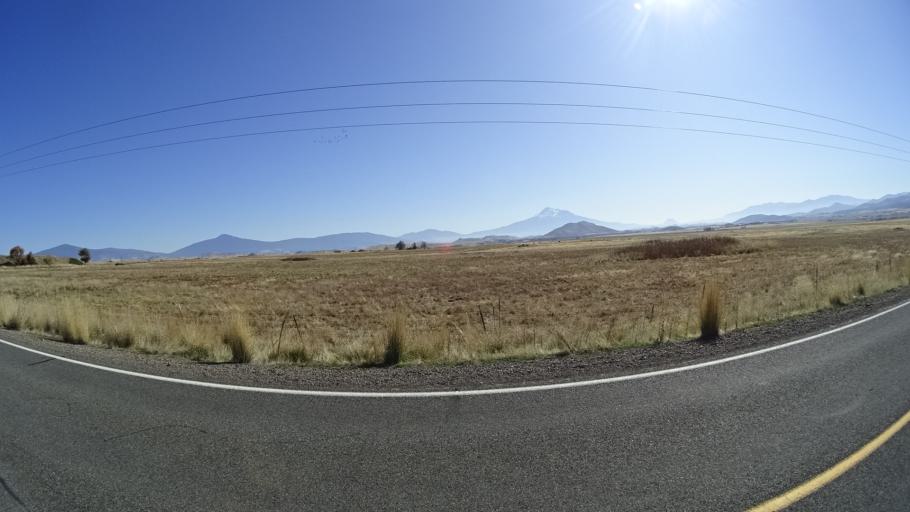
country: US
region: California
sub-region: Siskiyou County
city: Montague
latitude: 41.7632
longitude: -122.5582
